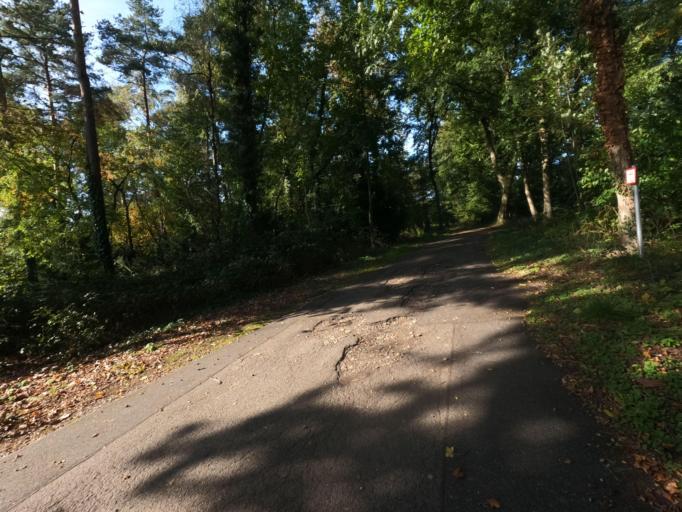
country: DE
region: North Rhine-Westphalia
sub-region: Regierungsbezirk Koln
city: Wassenberg
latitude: 51.0953
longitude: 6.1736
